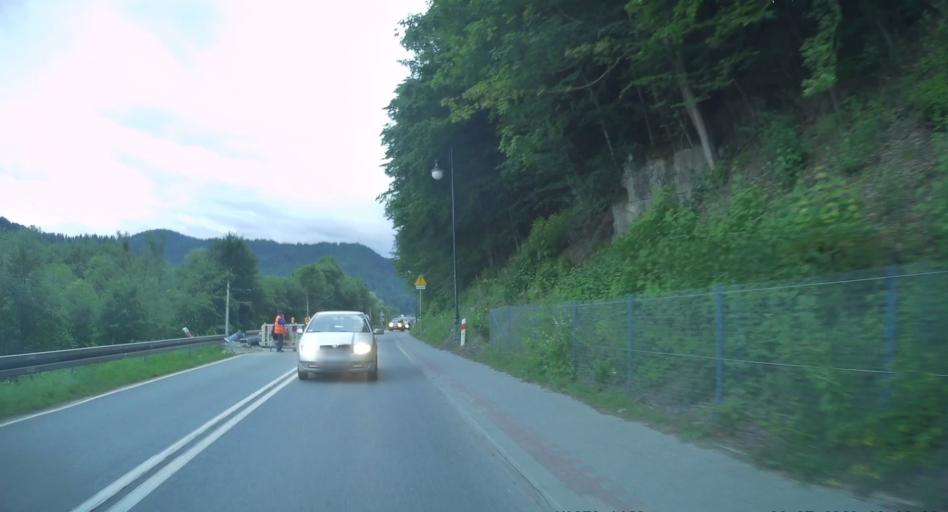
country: PL
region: Lesser Poland Voivodeship
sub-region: Powiat nowosadecki
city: Muszyna
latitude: 49.3505
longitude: 20.8842
